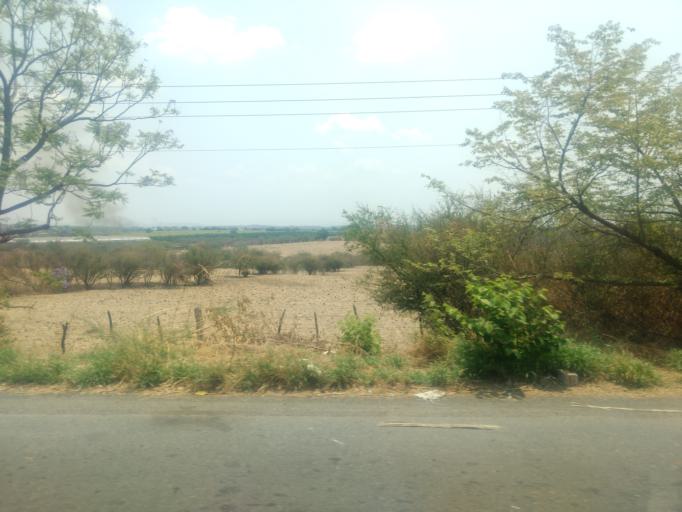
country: MX
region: Morelos
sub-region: Mazatepec
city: Cuauchichinola
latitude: 18.6322
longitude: -99.3776
